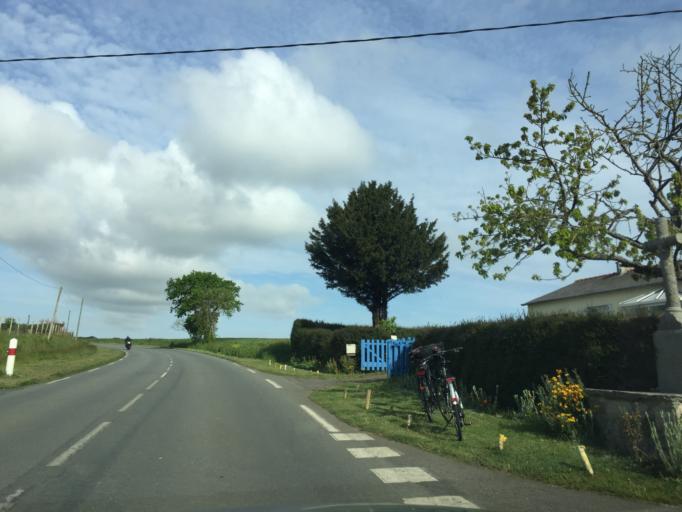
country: FR
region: Brittany
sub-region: Departement des Cotes-d'Armor
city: Matignon
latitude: 48.6145
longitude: -2.3299
